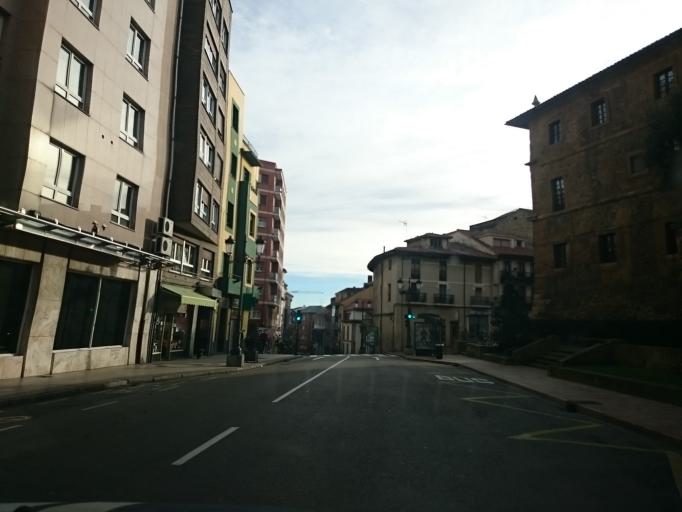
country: ES
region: Asturias
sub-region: Province of Asturias
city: Oviedo
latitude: 43.3640
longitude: -5.8393
